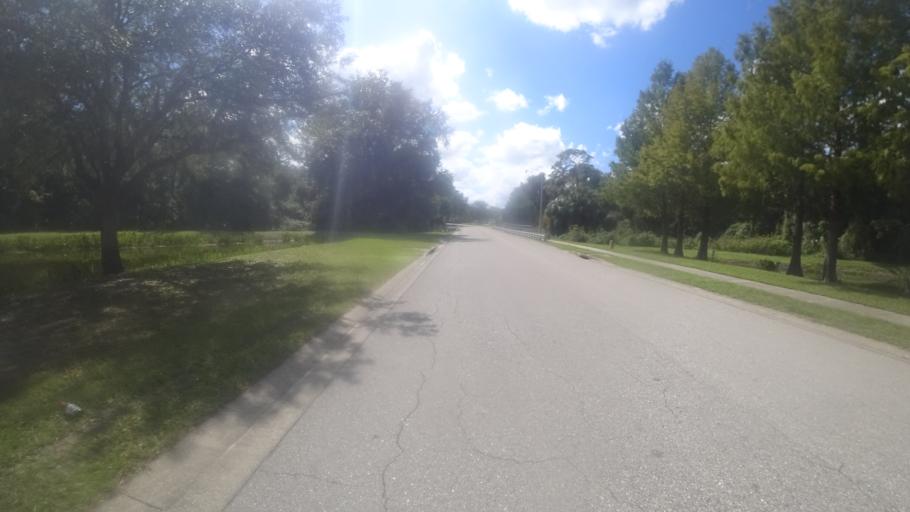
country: US
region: Florida
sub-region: Manatee County
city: Ellenton
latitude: 27.5066
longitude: -82.4013
